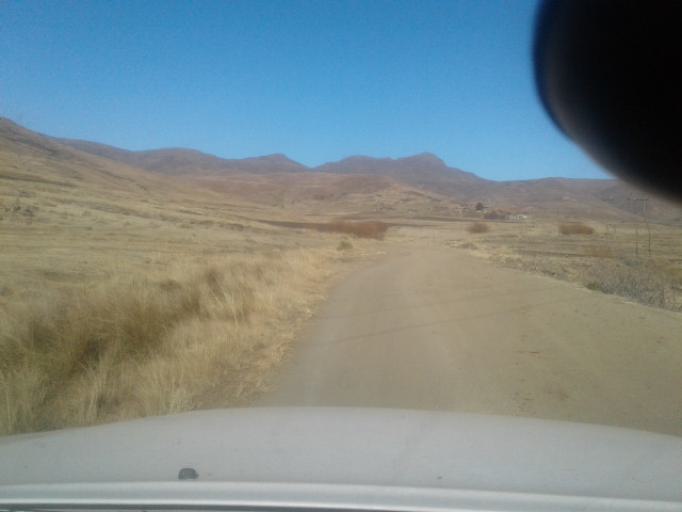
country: LS
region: Maseru
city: Nako
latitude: -29.3762
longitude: 28.0182
